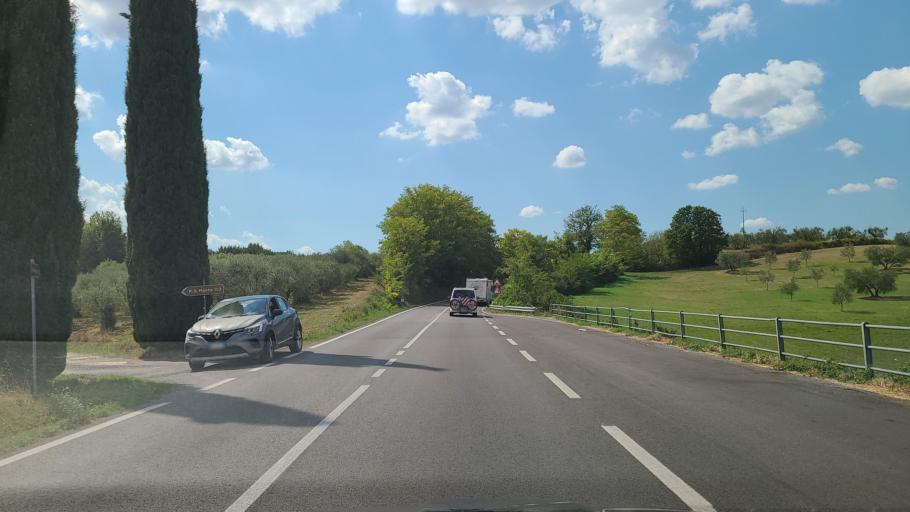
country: IT
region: Tuscany
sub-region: Provincia di Siena
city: Casole d'Elsa
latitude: 43.4058
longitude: 11.0480
